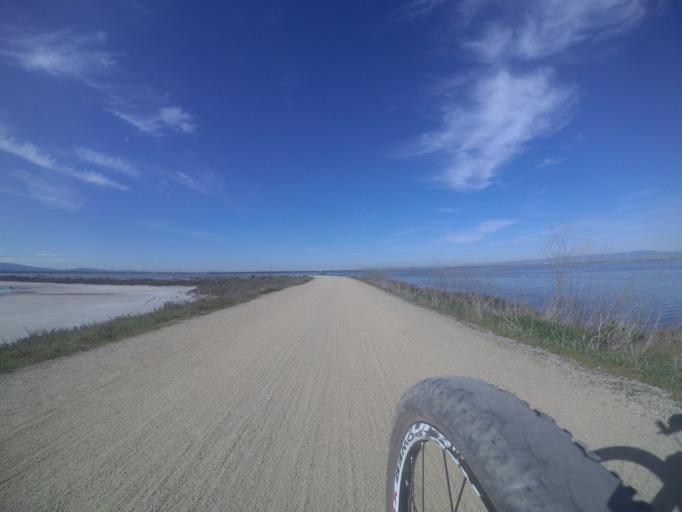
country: US
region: California
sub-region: Santa Clara County
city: Mountain View
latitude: 37.4355
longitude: -122.0539
